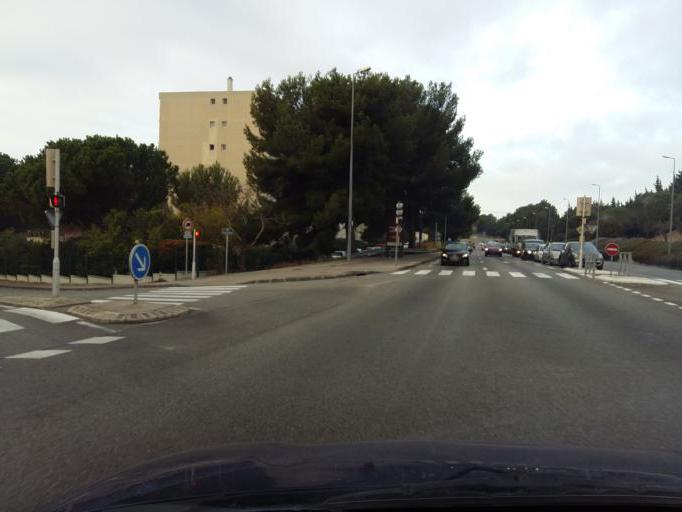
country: FR
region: Provence-Alpes-Cote d'Azur
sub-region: Departement des Bouches-du-Rhone
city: Martigues
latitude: 43.4117
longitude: 5.0438
